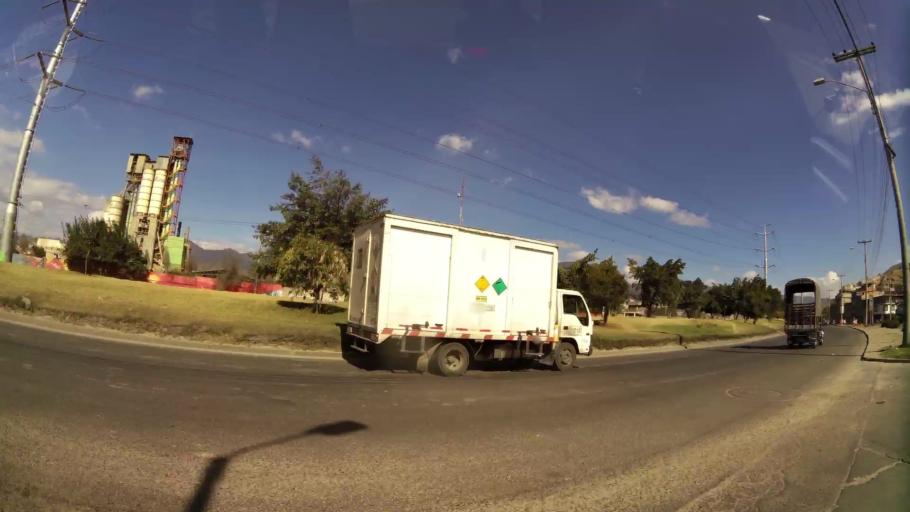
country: CO
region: Bogota D.C.
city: Bogota
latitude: 4.5470
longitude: -74.1372
